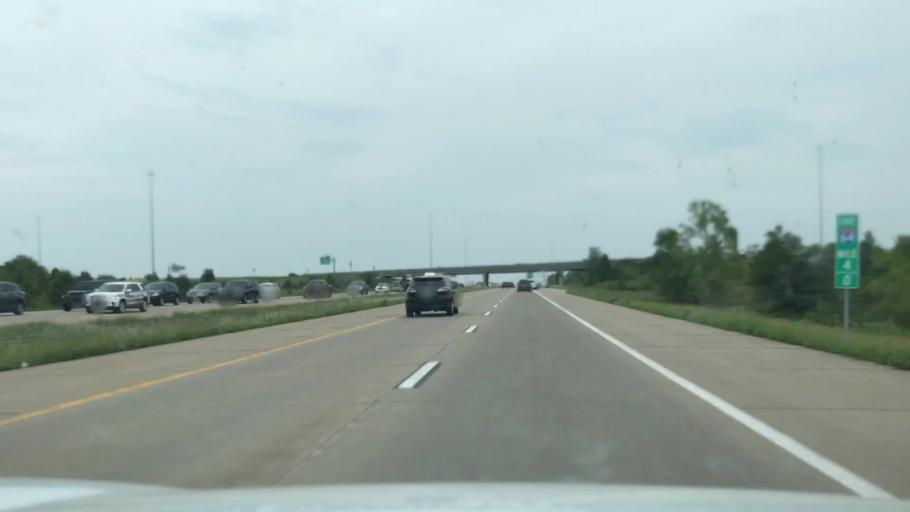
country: US
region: Missouri
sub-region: Saint Charles County
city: Lake Saint Louis
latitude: 38.7720
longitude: -90.7799
